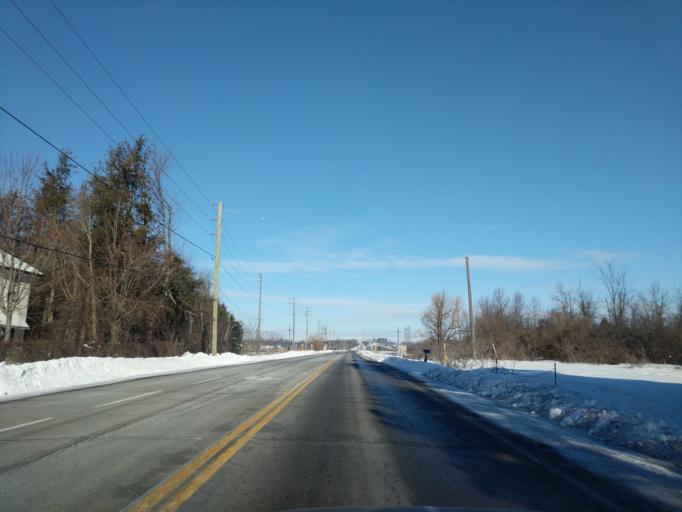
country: CA
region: Ontario
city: Pickering
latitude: 43.8358
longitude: -79.1449
